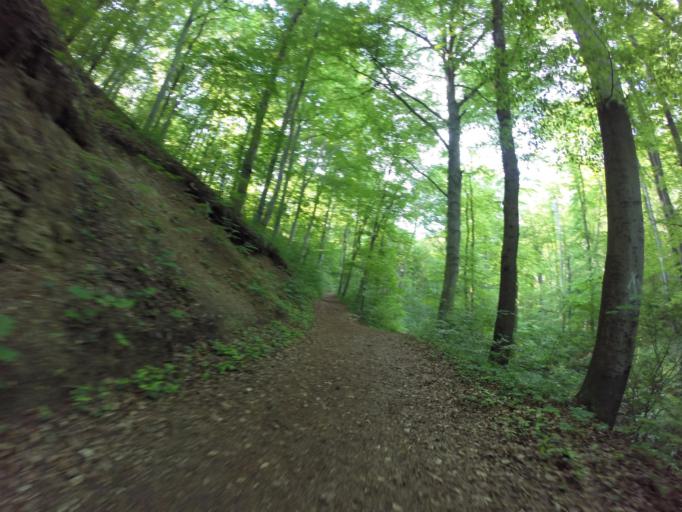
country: DE
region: Thuringia
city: Lehesten
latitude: 50.9594
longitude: 11.5923
